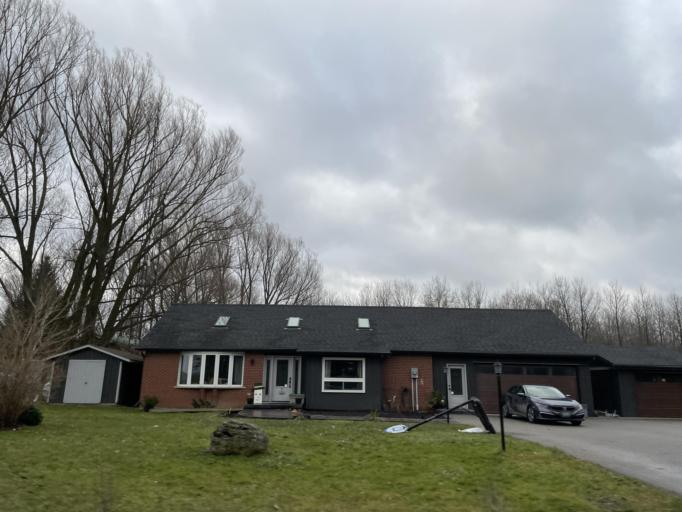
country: CA
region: Ontario
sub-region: Wellington County
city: Guelph
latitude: 43.5092
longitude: -80.3361
